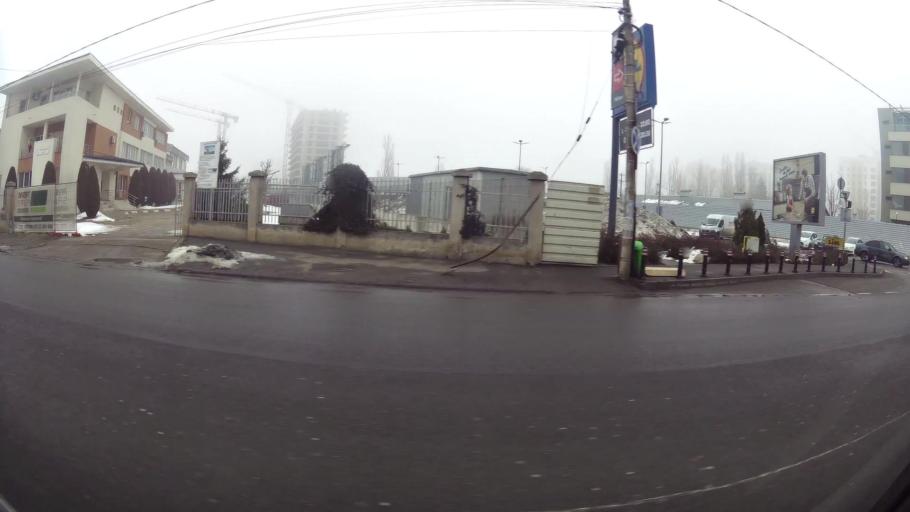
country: RO
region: Ilfov
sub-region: Comuna Chiajna
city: Rosu
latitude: 44.4439
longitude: 26.0195
